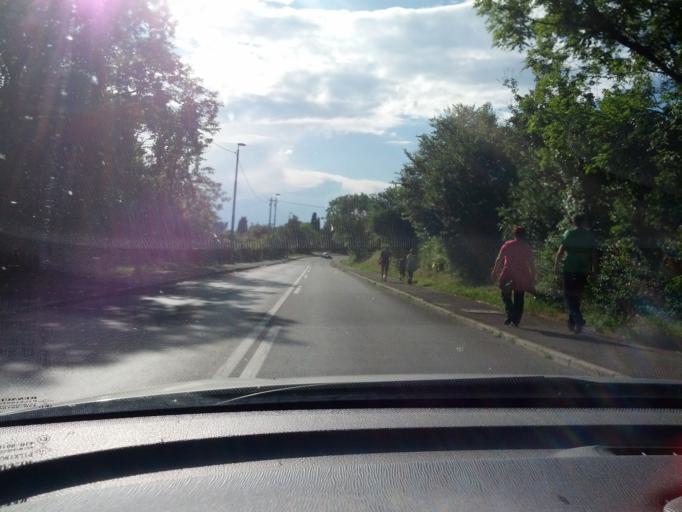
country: SI
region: Koper-Capodistria
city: Ankaran
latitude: 45.5756
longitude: 13.7407
